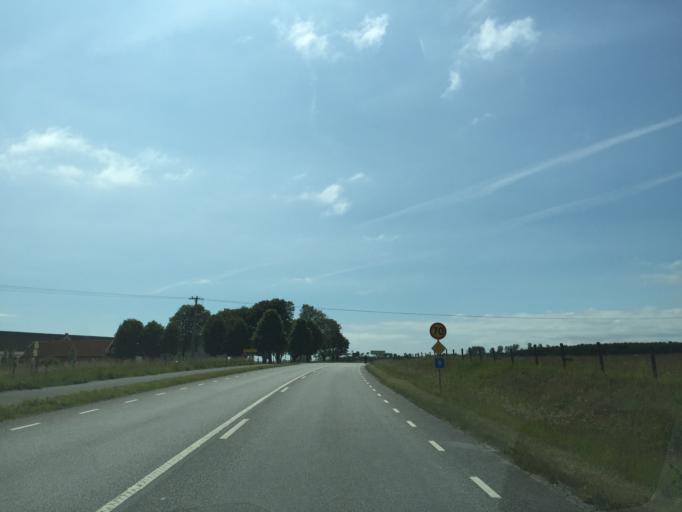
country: SE
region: Skane
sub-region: Ystads Kommun
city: Kopingebro
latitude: 55.4318
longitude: 13.9716
